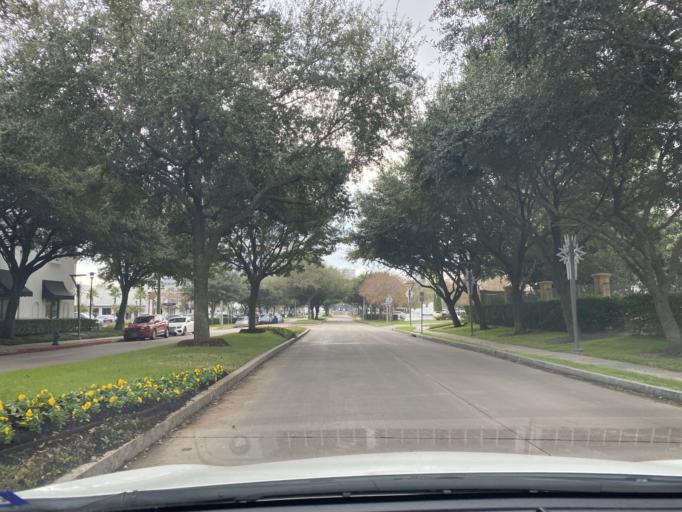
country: US
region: Texas
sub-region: Harris County
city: Hunters Creek Village
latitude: 29.7565
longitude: -95.4578
